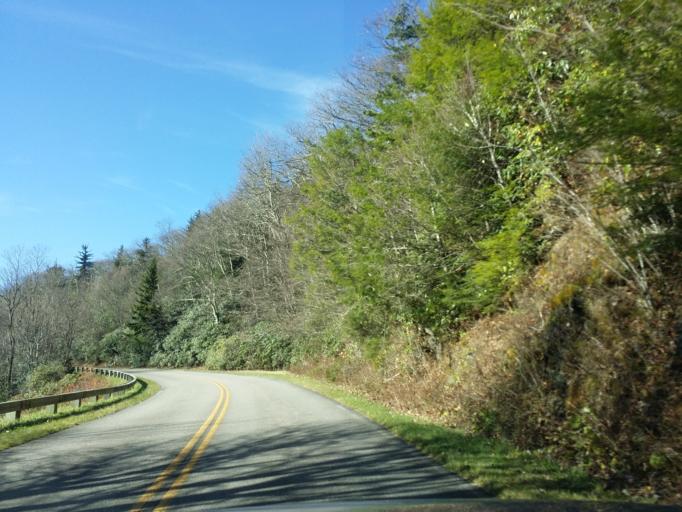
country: US
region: North Carolina
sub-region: Buncombe County
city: Black Mountain
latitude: 35.7232
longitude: -82.2134
